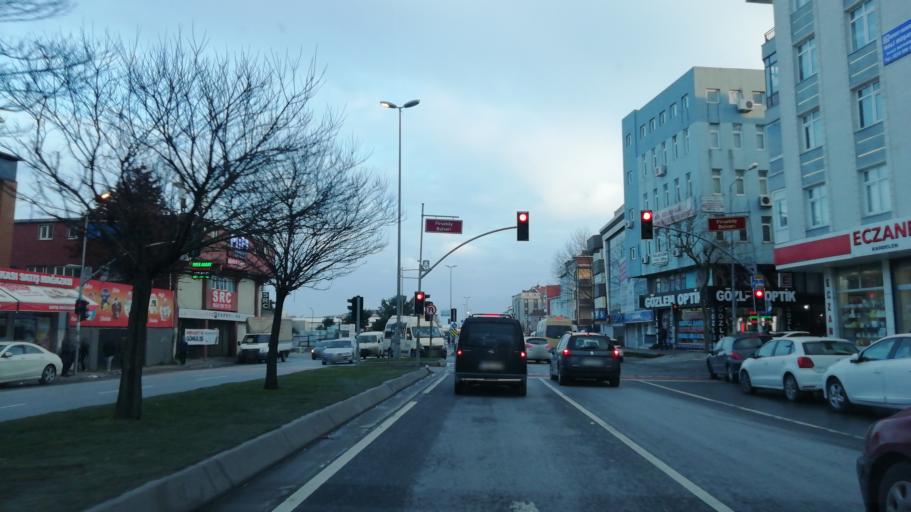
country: TR
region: Istanbul
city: Yakuplu
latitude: 41.0057
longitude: 28.7064
